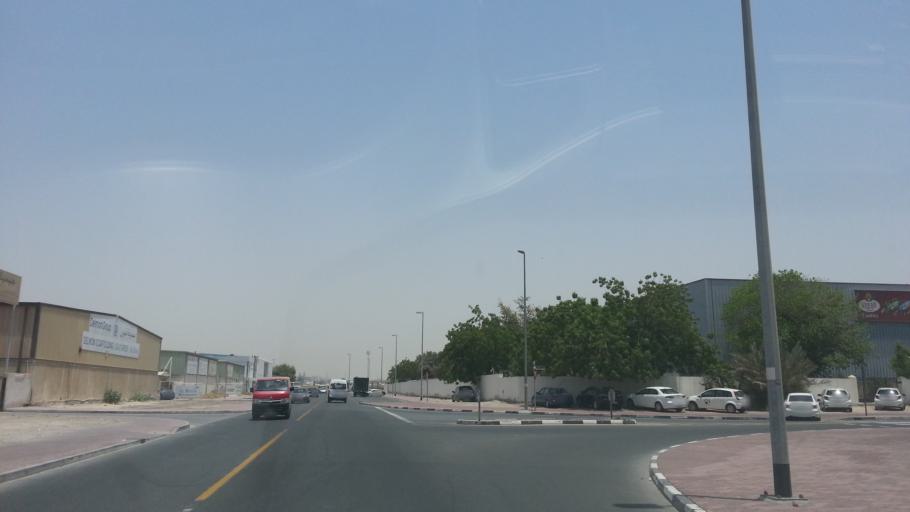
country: AE
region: Dubai
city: Dubai
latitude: 25.1526
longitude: 55.2281
